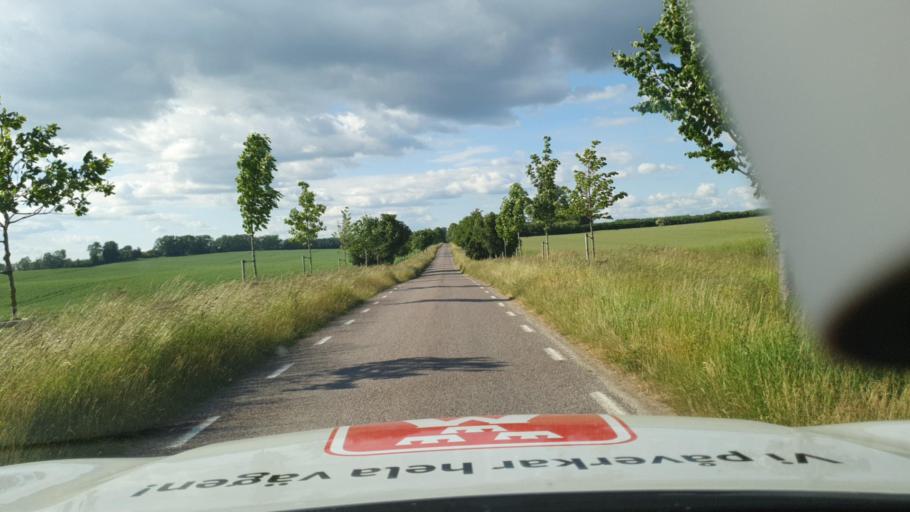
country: SE
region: Skane
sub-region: Ystads Kommun
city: Ystad
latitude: 55.4360
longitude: 13.7366
